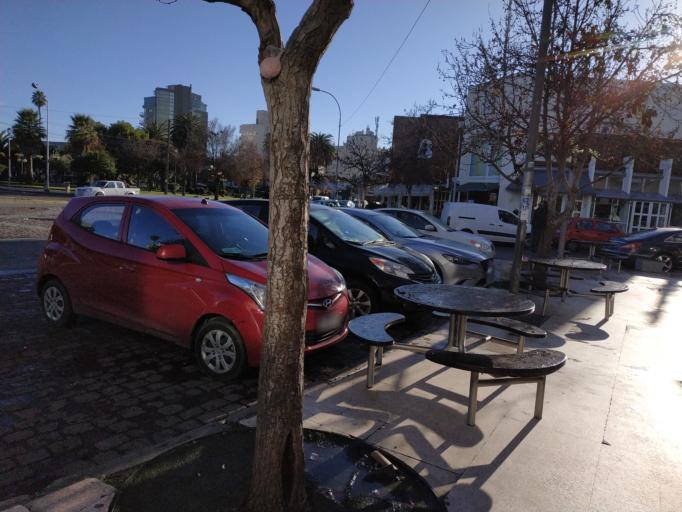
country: CL
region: Valparaiso
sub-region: Provincia de Valparaiso
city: Vina del Mar
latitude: -33.0185
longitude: -71.5587
